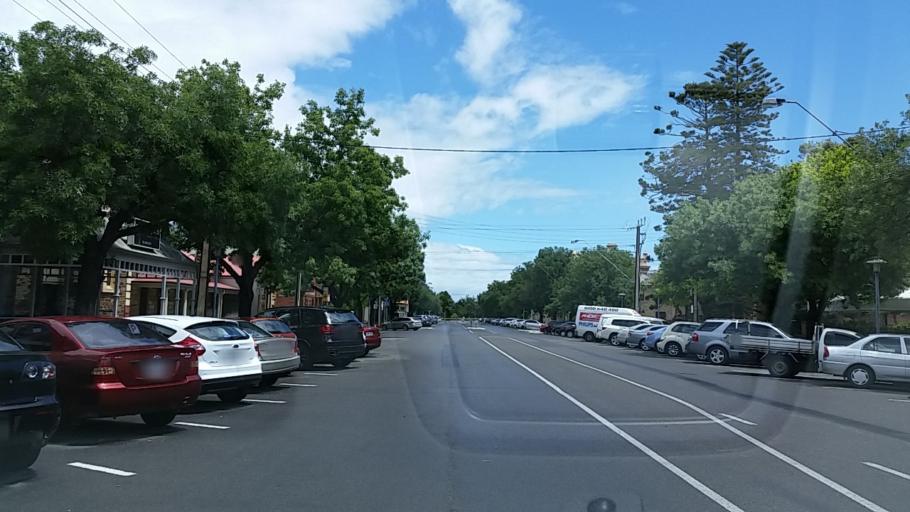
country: AU
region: South Australia
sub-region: Adelaide
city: North Adelaide
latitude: -34.9061
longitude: 138.5954
